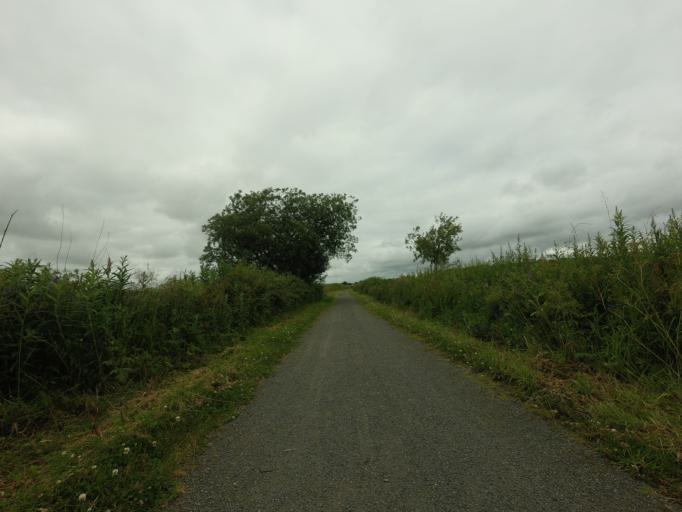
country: GB
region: Scotland
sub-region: Aberdeenshire
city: Ellon
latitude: 57.4827
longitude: -2.1344
